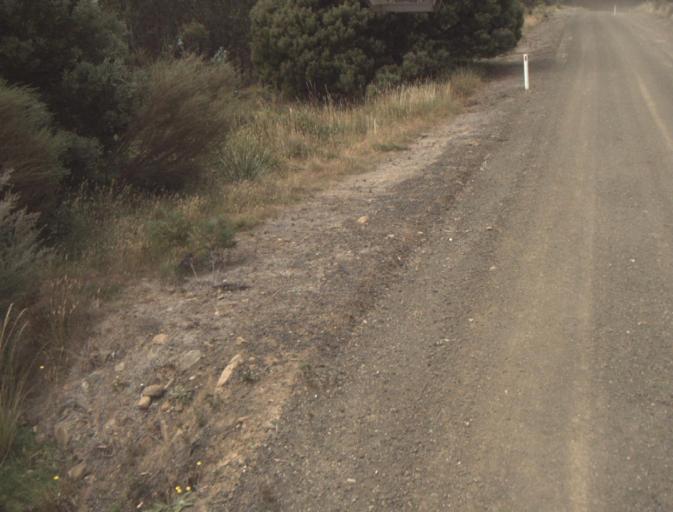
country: AU
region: Tasmania
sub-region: Northern Midlands
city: Evandale
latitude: -41.4522
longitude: 147.4430
